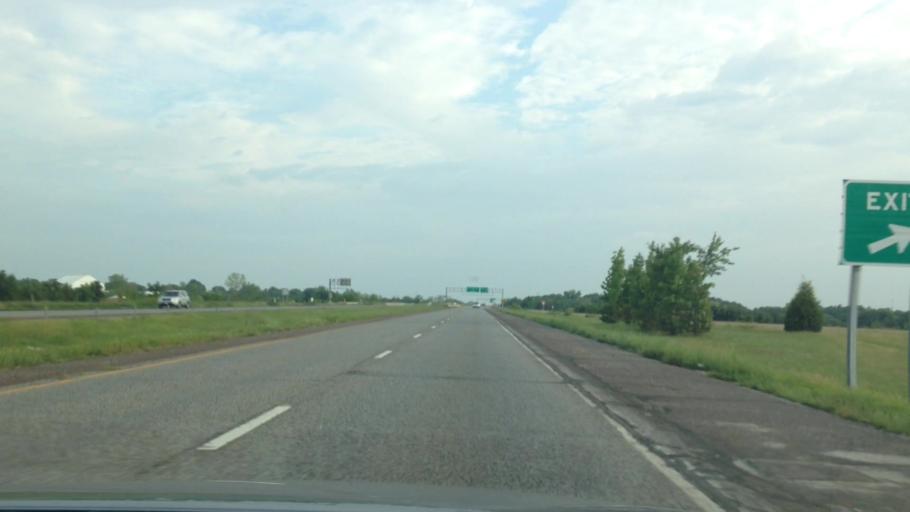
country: US
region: Missouri
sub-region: Clay County
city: Smithville
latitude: 39.3134
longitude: -94.5846
